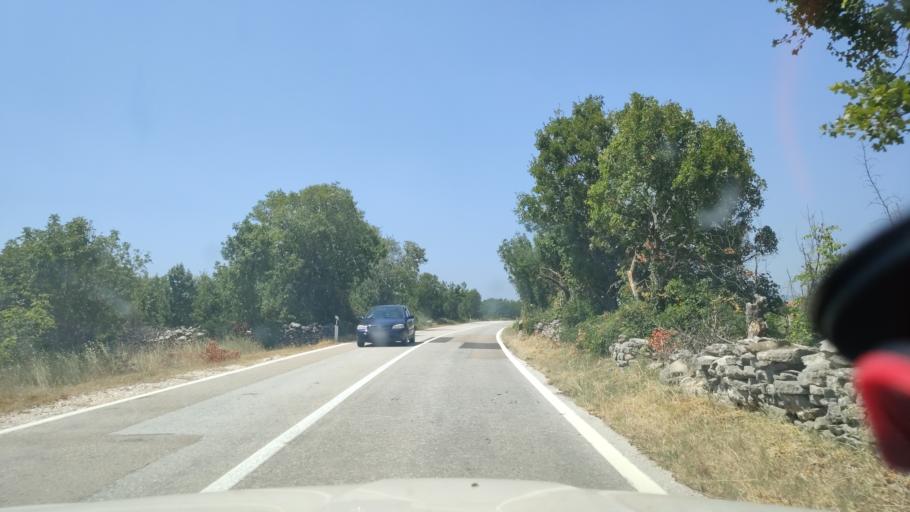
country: HR
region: Sibensko-Kniniska
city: Kistanje
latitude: 43.9743
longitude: 15.9179
